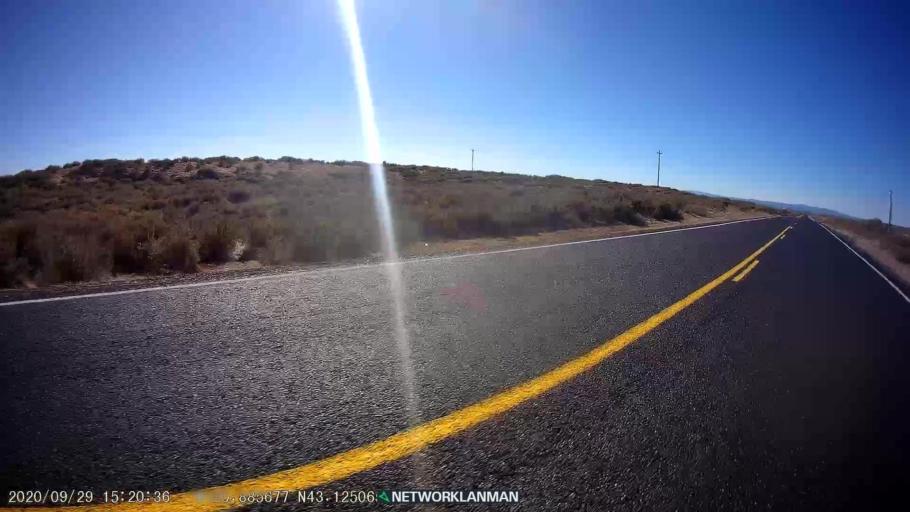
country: US
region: Oregon
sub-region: Deschutes County
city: La Pine
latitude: 43.1252
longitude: -120.8860
